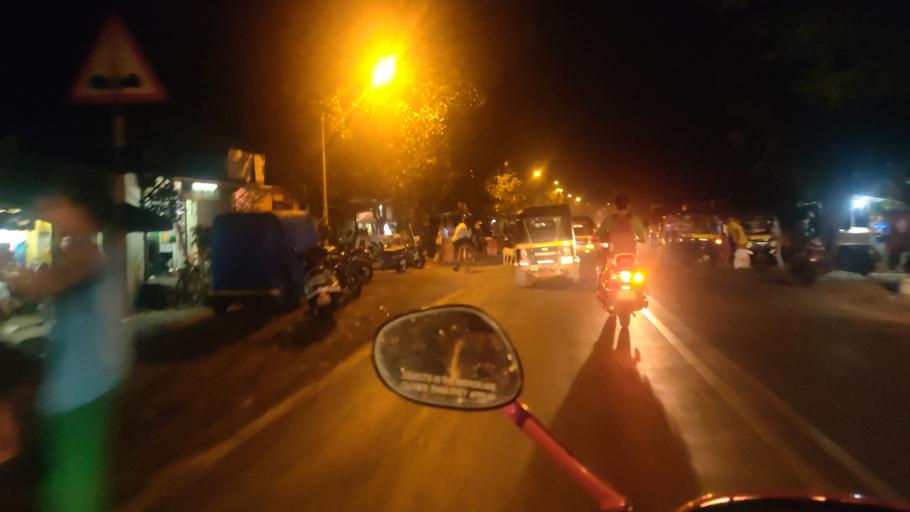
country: IN
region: Maharashtra
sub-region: Thane
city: Bhayandar
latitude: 19.2992
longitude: 72.8356
